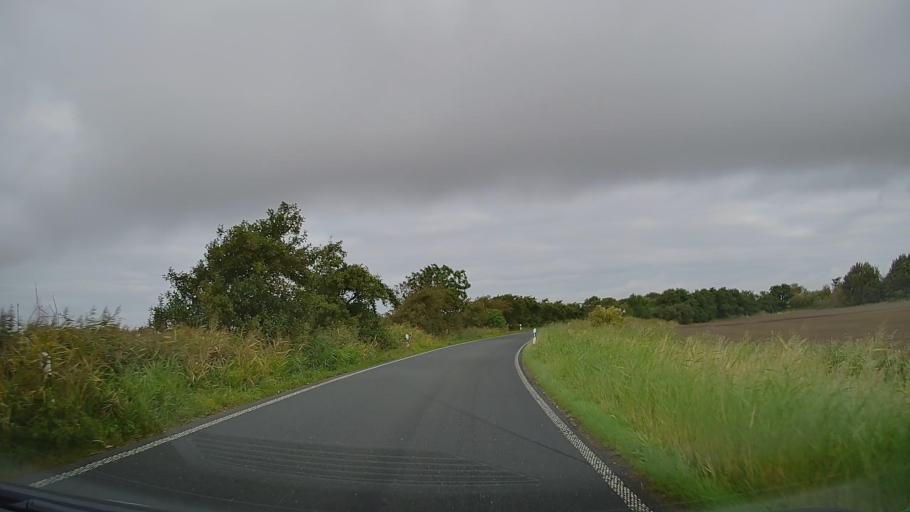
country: DE
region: Schleswig-Holstein
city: Galmsbull
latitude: 54.7697
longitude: 8.7158
